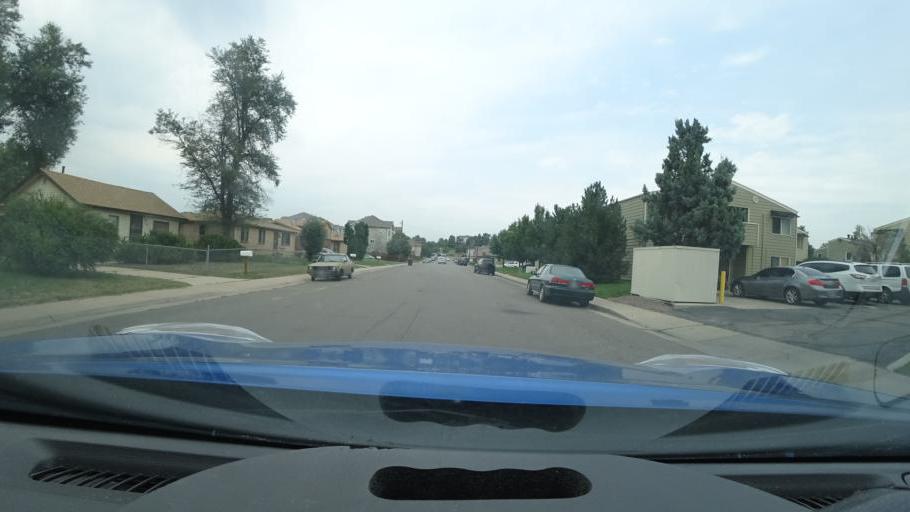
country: US
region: Colorado
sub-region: Arapahoe County
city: Glendale
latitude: 39.7012
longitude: -104.9141
